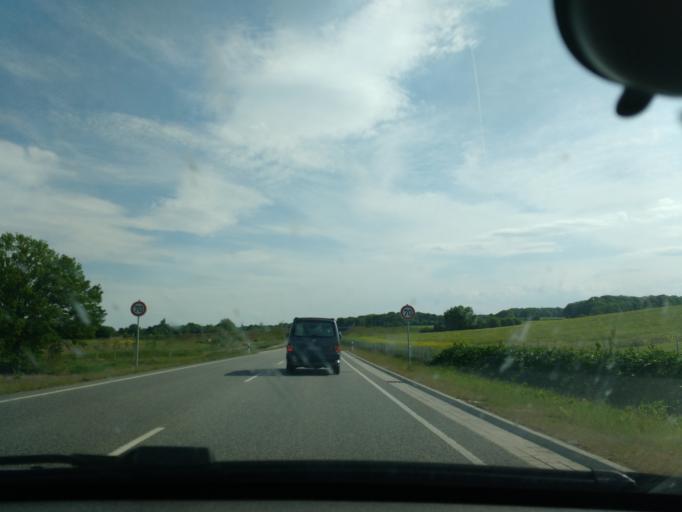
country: DE
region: Schleswig-Holstein
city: Pogeez
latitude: 53.7568
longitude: 10.7253
